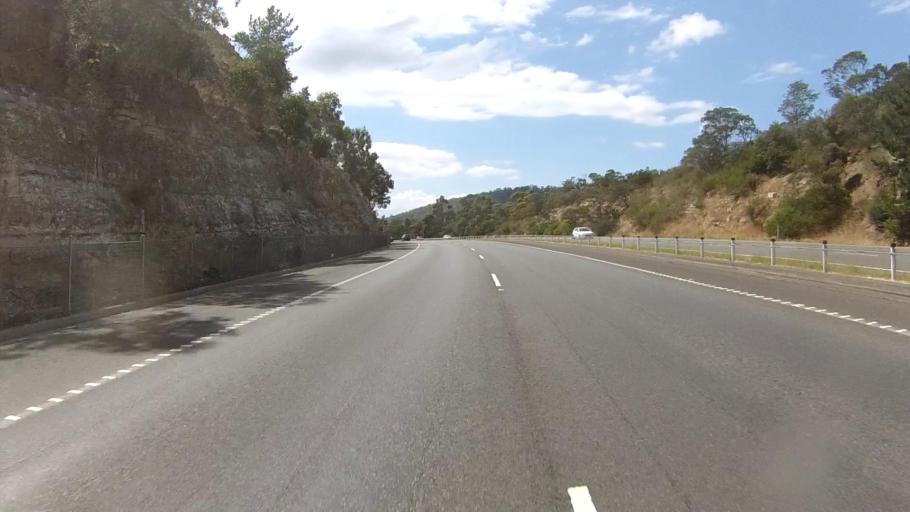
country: AU
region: Tasmania
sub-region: Clarence
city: Warrane
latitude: -42.8550
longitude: 147.4167
